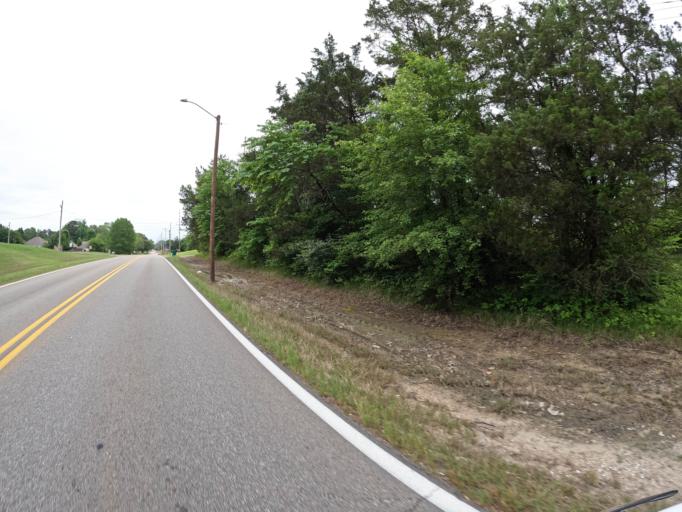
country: US
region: Mississippi
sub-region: Lee County
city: Tupelo
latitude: 34.2647
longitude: -88.7508
